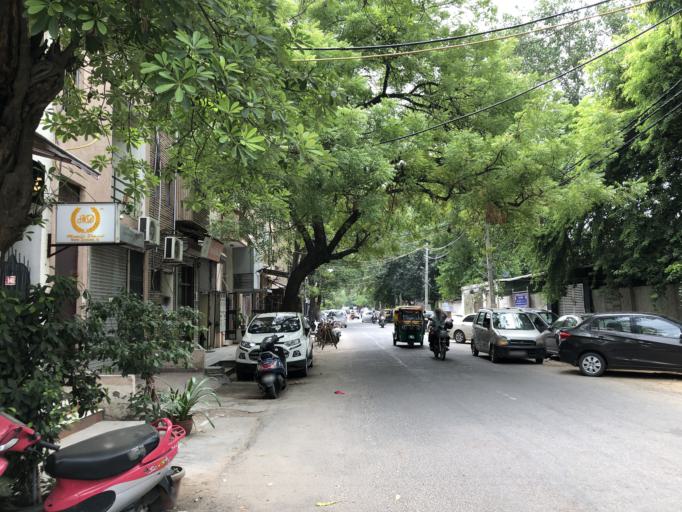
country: IN
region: NCT
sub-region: New Delhi
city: New Delhi
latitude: 28.5786
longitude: 77.2406
